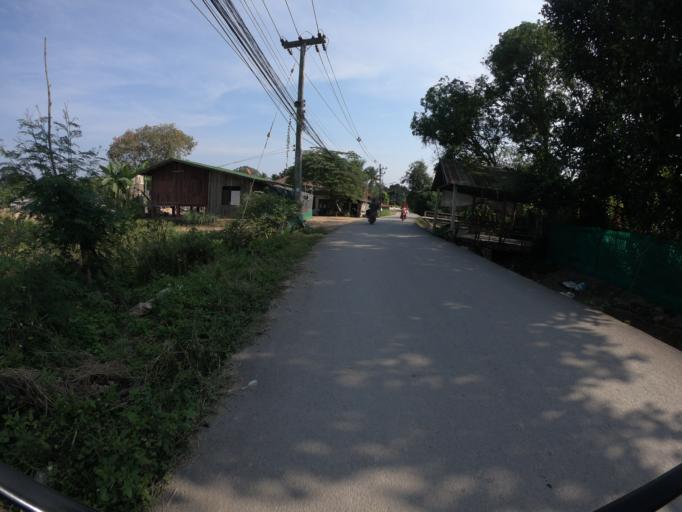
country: TH
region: Chiang Mai
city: Chiang Mai
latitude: 18.8345
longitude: 98.9951
